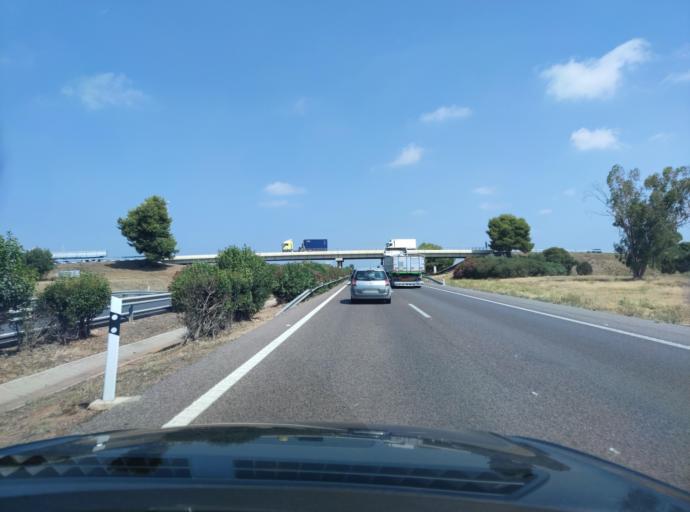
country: ES
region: Valencia
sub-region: Provincia de Castello
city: Alquerias del Nino Perdido
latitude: 39.8965
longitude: -0.1307
